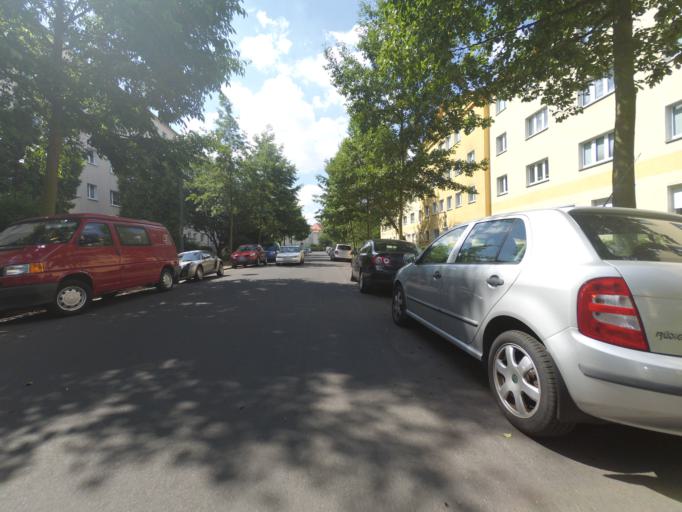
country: DE
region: Saxony
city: Albertstadt
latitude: 51.0360
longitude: 13.7986
